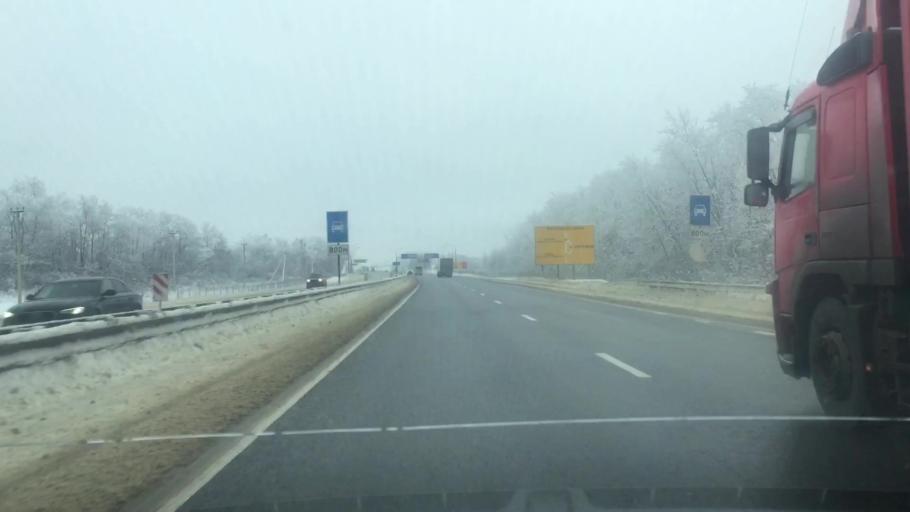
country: RU
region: Tula
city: Kazachka
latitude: 53.2982
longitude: 38.1780
